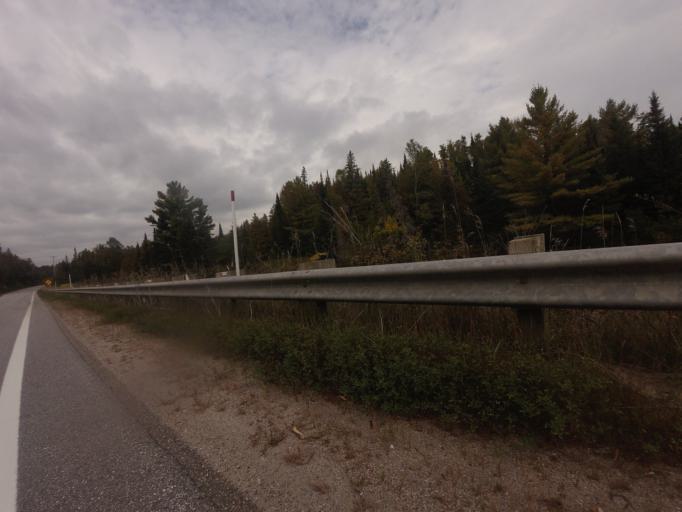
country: CA
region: Quebec
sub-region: Outaouais
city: Wakefield
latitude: 45.9327
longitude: -75.9887
